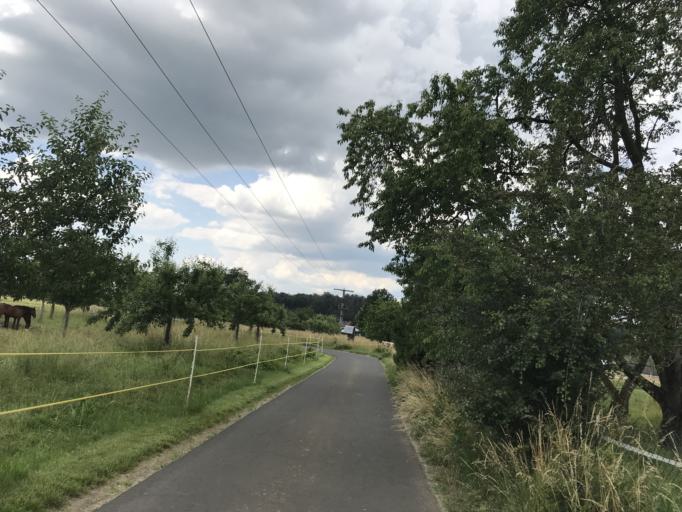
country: DE
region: Hesse
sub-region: Regierungsbezirk Giessen
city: Hungen
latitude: 50.4682
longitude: 8.9521
